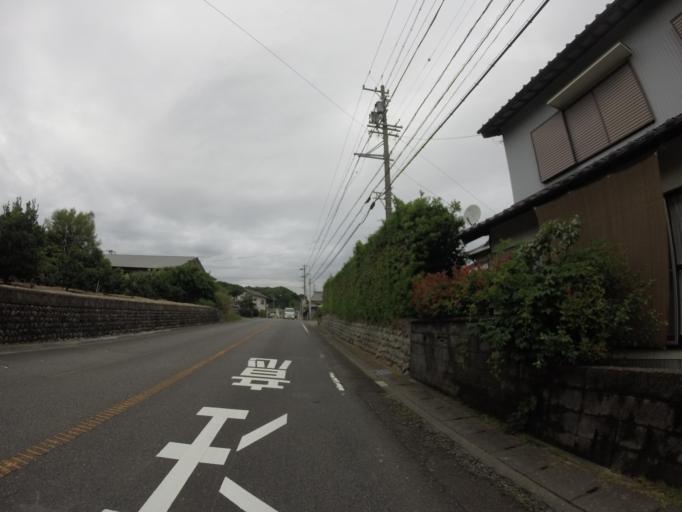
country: JP
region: Shizuoka
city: Sagara
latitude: 34.7323
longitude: 138.1615
